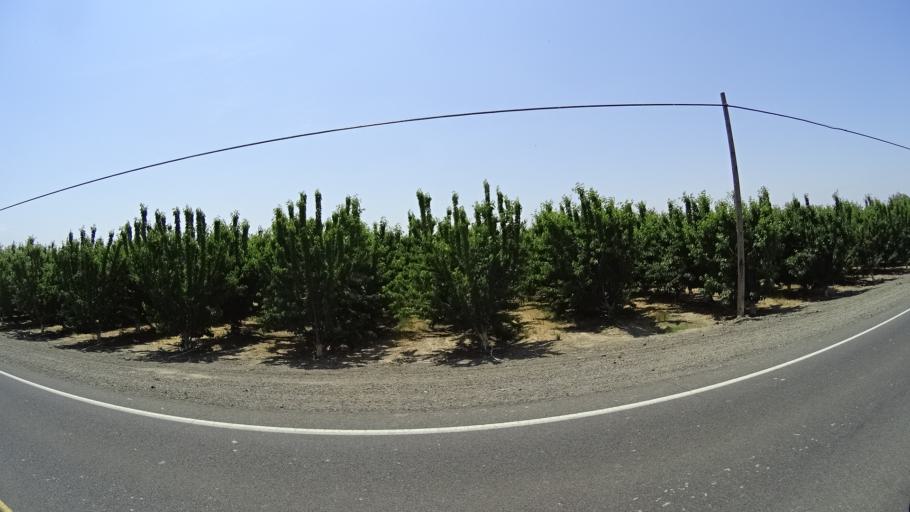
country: US
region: California
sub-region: Kings County
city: Armona
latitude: 36.3135
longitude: -119.7353
